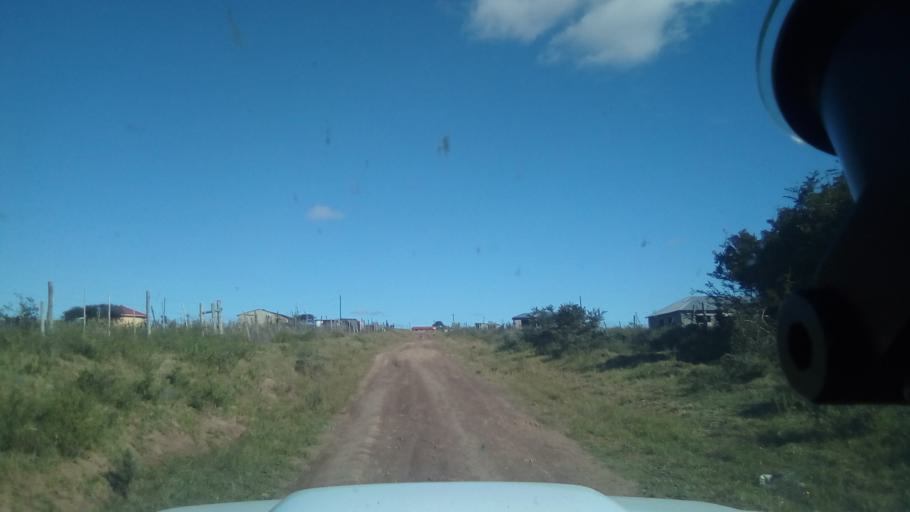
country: ZA
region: Eastern Cape
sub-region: Buffalo City Metropolitan Municipality
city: Bhisho
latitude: -32.7791
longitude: 27.3387
